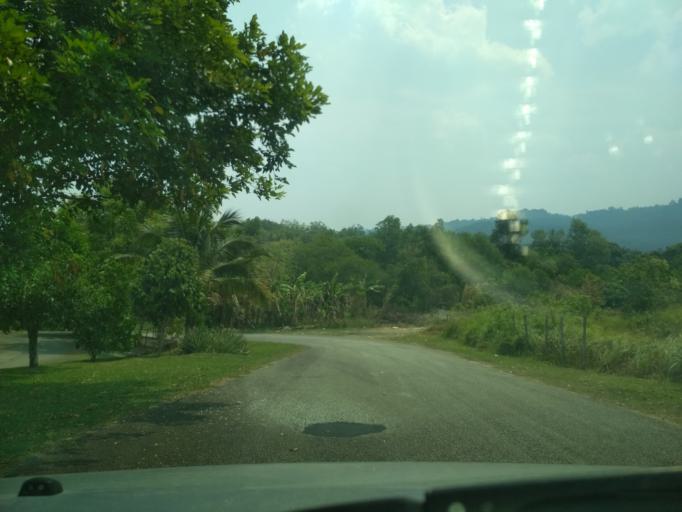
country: MY
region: Kedah
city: Kulim
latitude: 5.3560
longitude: 100.5271
